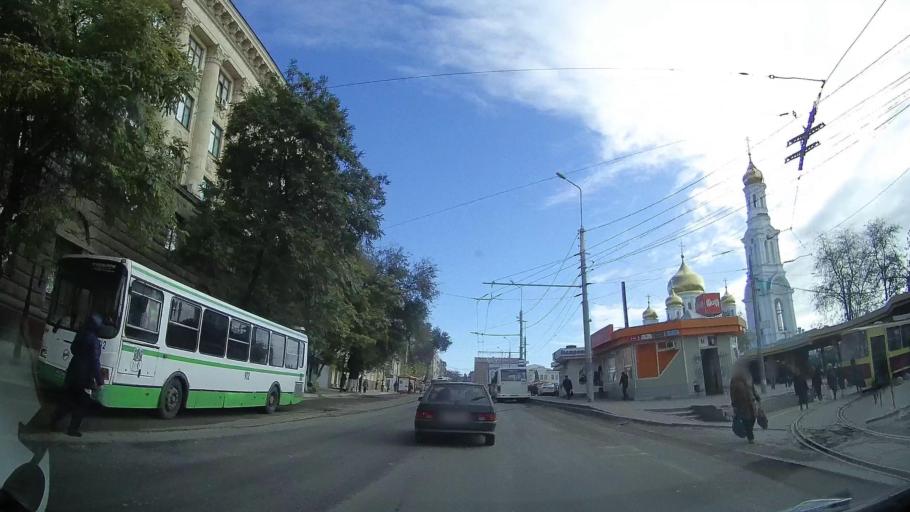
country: RU
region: Rostov
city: Rostov-na-Donu
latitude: 47.2176
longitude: 39.7095
